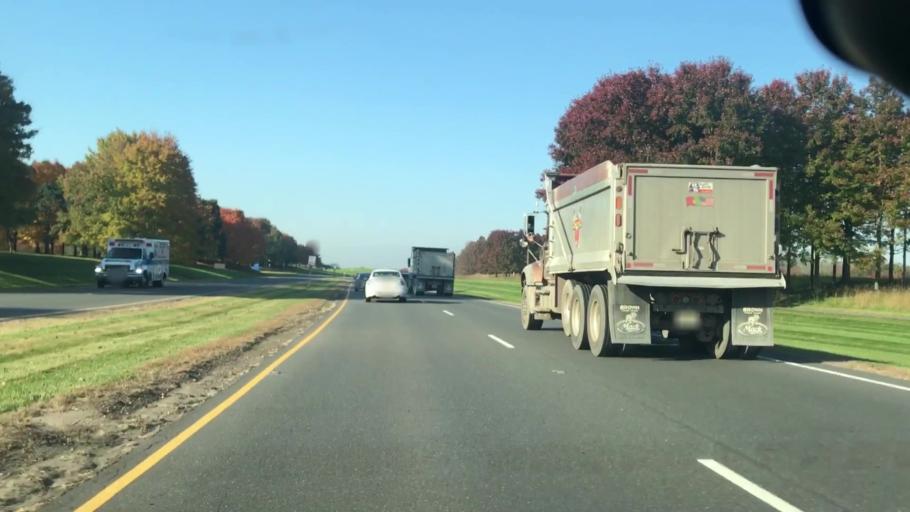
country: US
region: New Jersey
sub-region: Middlesex County
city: Plainsboro Center
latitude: 40.3407
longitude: -74.6059
